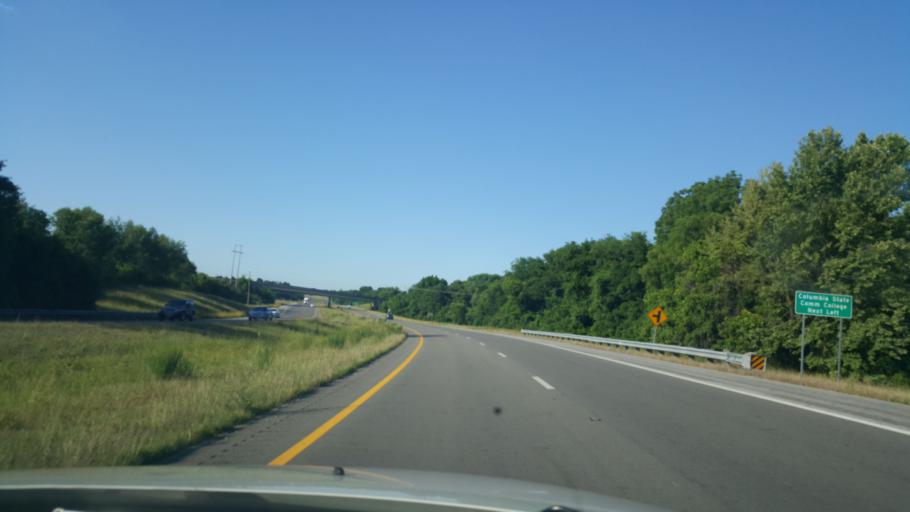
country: US
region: Tennessee
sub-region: Maury County
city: Columbia
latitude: 35.6200
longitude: -87.1191
